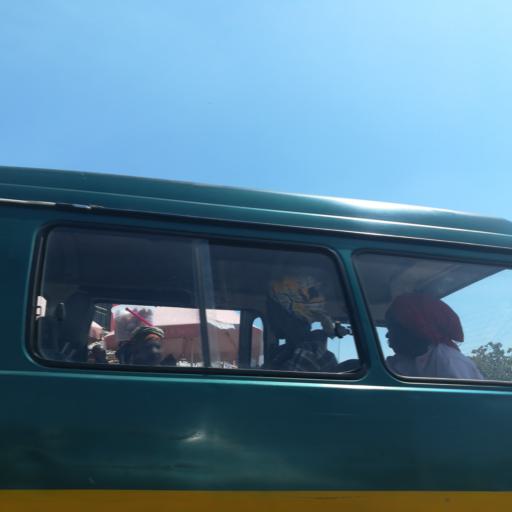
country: NG
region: Plateau
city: Bukuru
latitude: 9.7938
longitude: 8.8652
